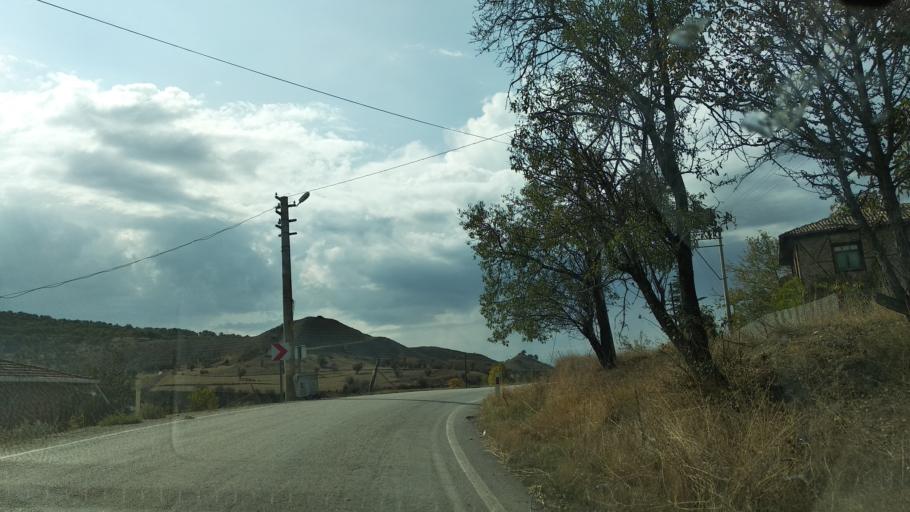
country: TR
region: Bolu
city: Seben
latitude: 40.4048
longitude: 31.5682
